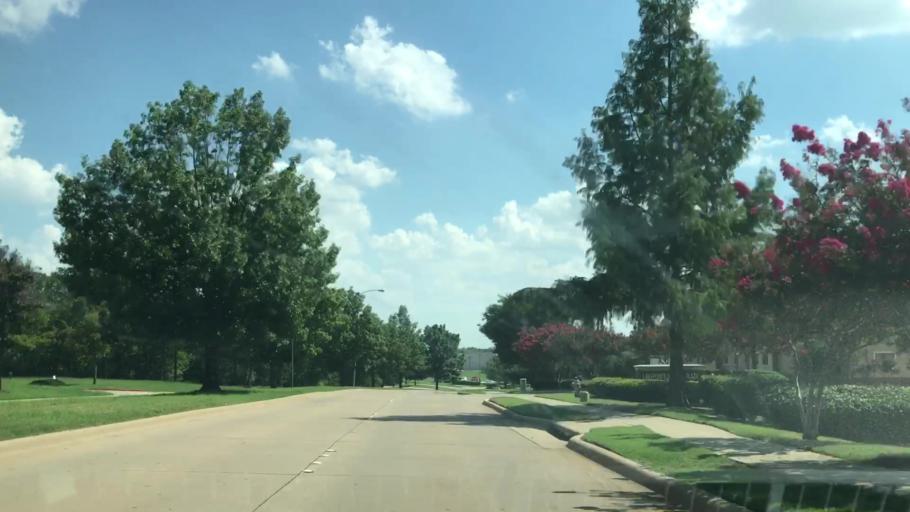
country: US
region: Texas
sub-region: Denton County
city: Lewisville
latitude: 33.0176
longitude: -96.9788
